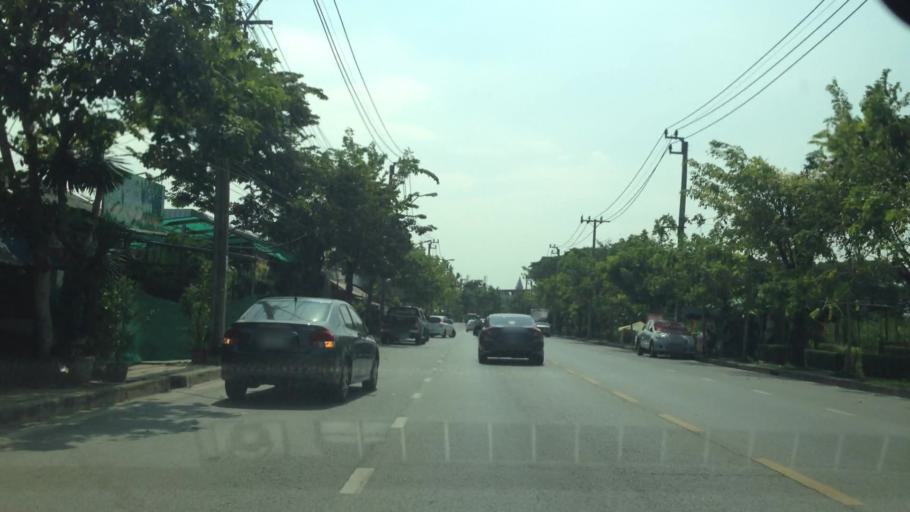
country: TH
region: Bangkok
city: Bang Khen
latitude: 13.8844
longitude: 100.6437
